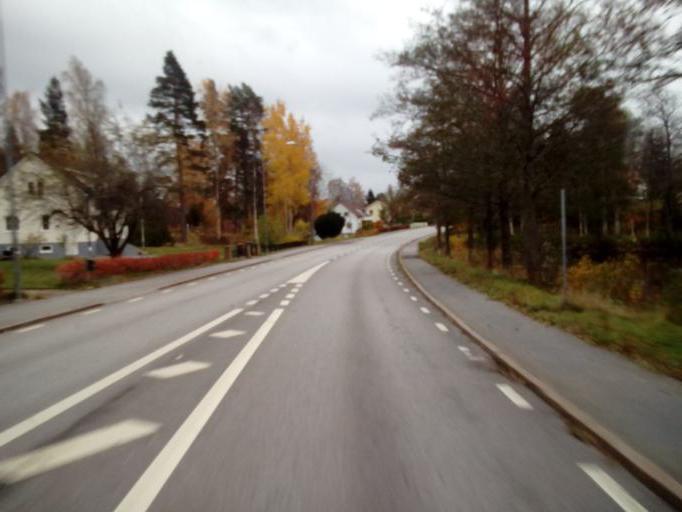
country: SE
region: OErebro
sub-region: Degerfors Kommun
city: Degerfors
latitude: 59.1301
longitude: 14.5175
